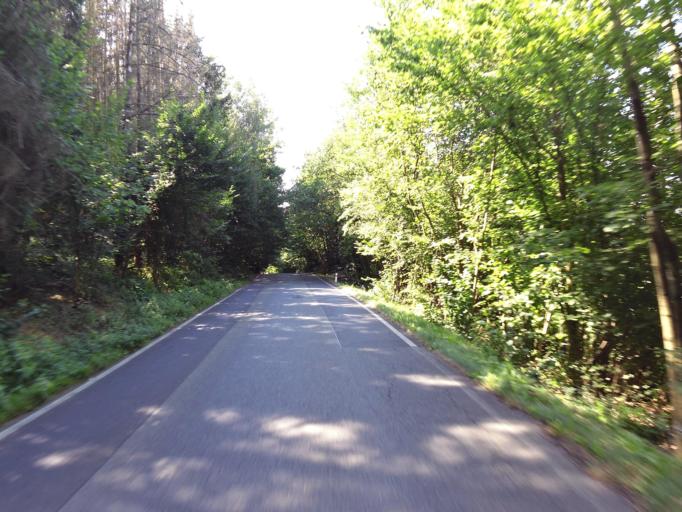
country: CZ
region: Central Bohemia
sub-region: Okres Praha-Vychod
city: Mnichovice
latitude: 49.9480
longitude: 14.7295
